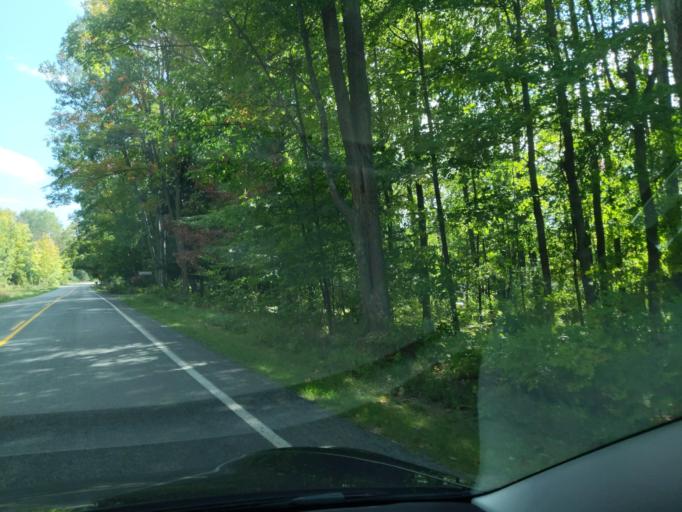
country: US
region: Michigan
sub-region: Antrim County
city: Bellaire
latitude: 44.9917
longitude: -85.2860
